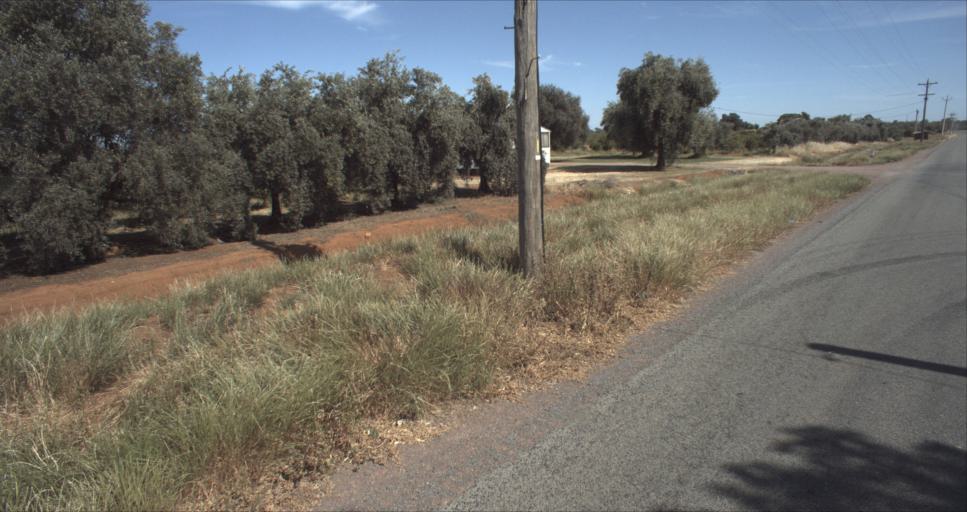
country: AU
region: New South Wales
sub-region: Leeton
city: Leeton
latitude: -34.5857
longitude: 146.4719
